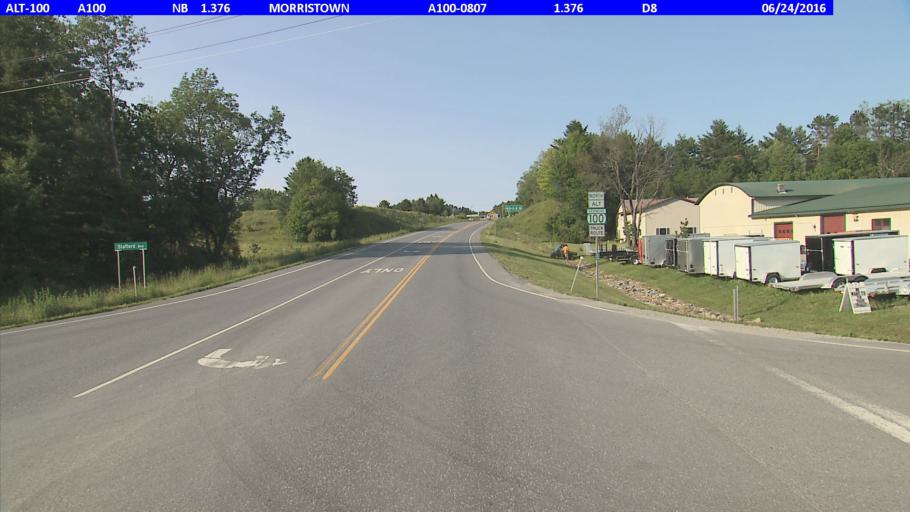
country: US
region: Vermont
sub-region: Lamoille County
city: Morrisville
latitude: 44.5741
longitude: -72.5970
